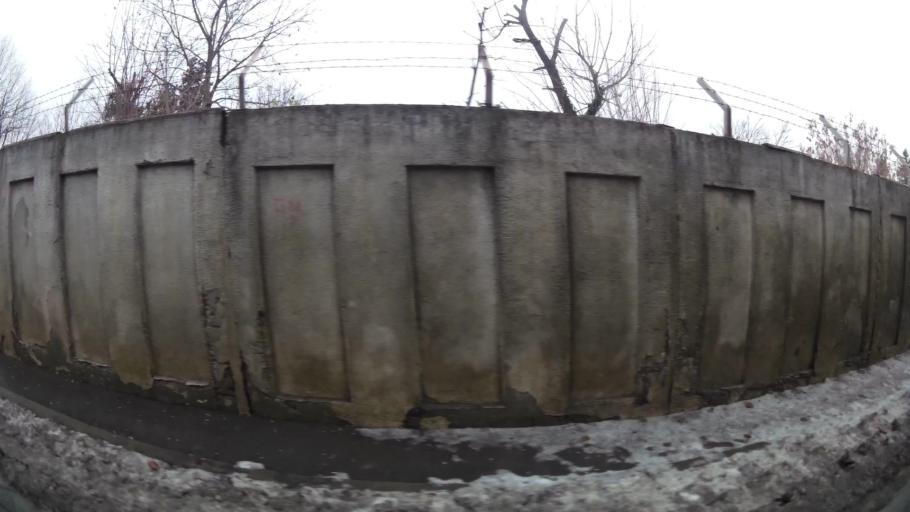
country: RO
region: Bucuresti
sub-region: Municipiul Bucuresti
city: Bucuresti
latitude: 44.4606
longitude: 26.0627
